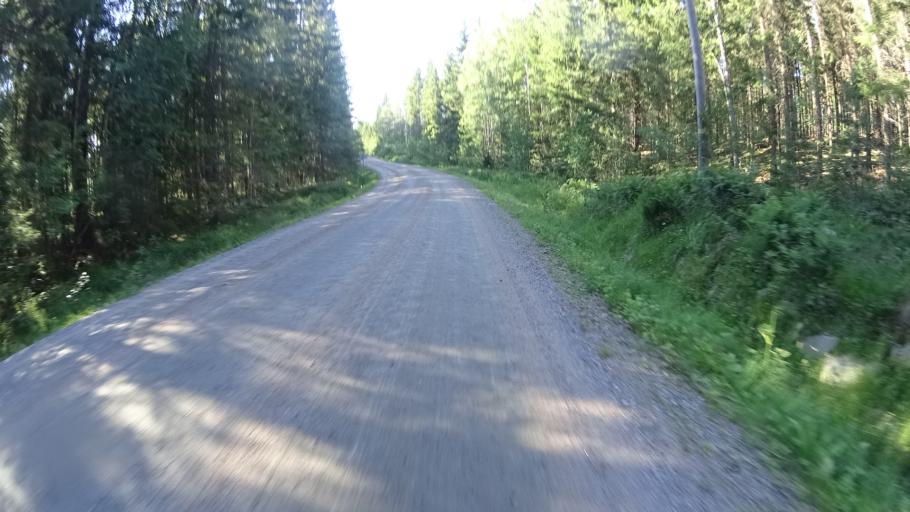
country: FI
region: Uusimaa
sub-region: Helsinki
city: Karkkila
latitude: 60.6493
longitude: 24.1264
